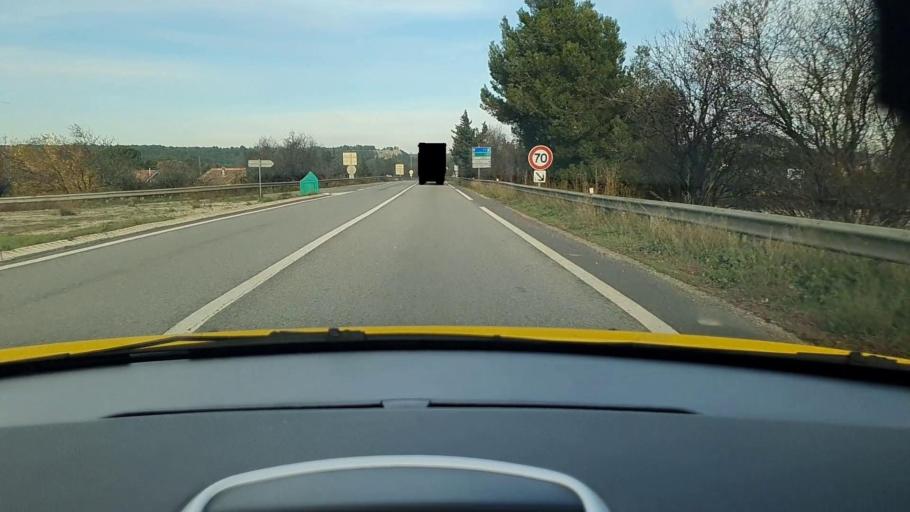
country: FR
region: Languedoc-Roussillon
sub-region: Departement du Gard
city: Beaucaire
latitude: 43.7972
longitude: 4.6093
